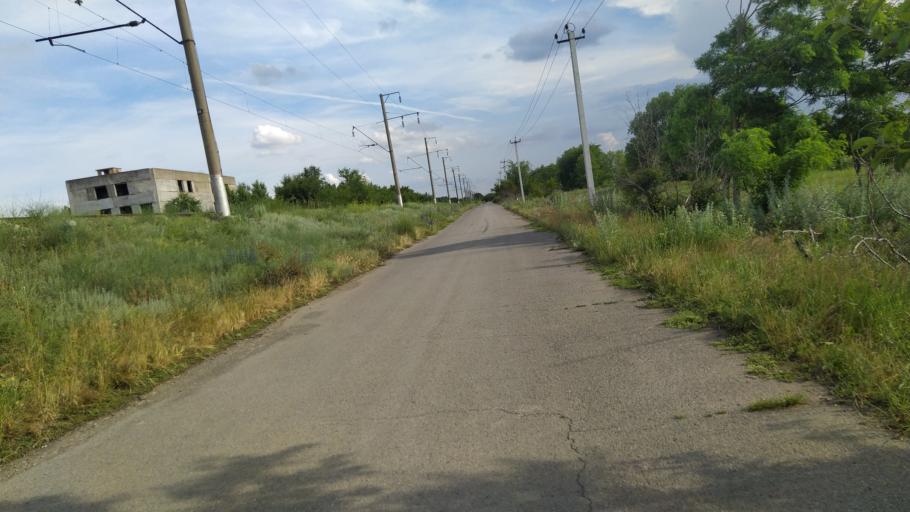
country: RU
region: Rostov
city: Bataysk
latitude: 47.1159
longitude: 39.7114
